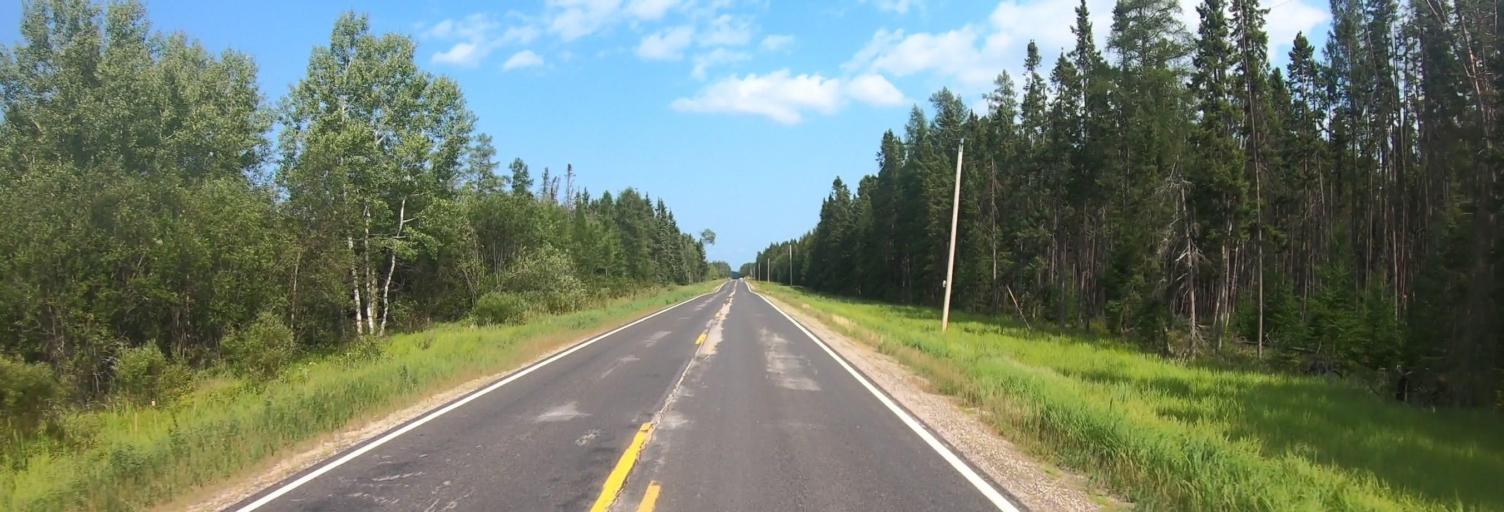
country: US
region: Minnesota
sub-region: Saint Louis County
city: Mountain Iron
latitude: 47.8913
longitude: -92.6695
